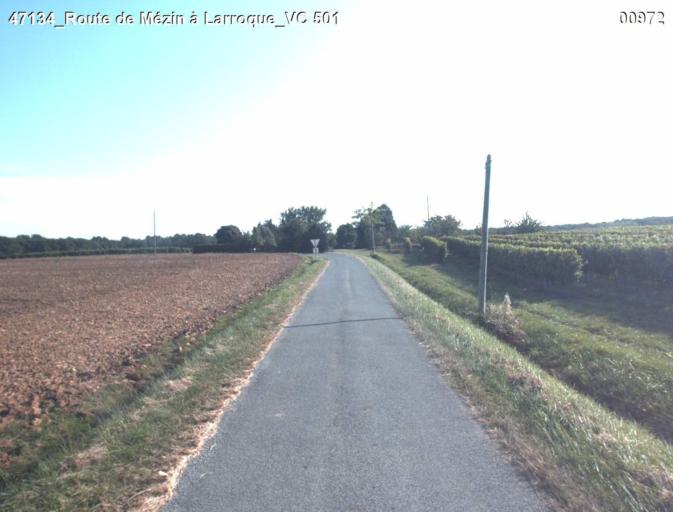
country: FR
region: Aquitaine
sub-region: Departement du Lot-et-Garonne
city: Mezin
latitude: 44.0065
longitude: 0.2758
